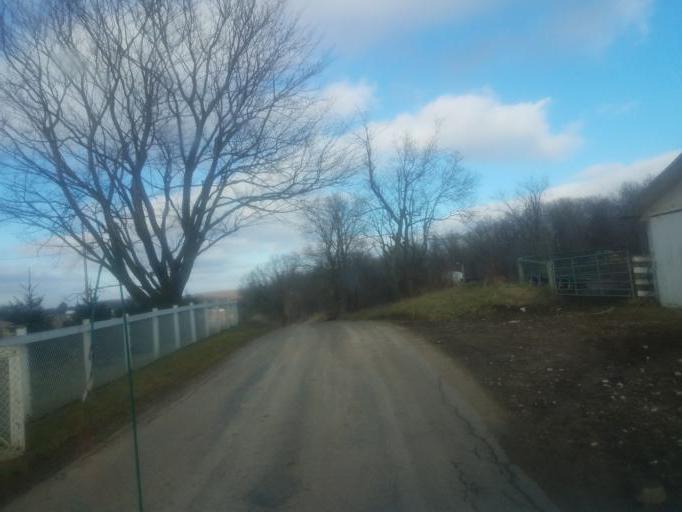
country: US
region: Ohio
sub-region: Sandusky County
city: Bellville
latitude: 40.5846
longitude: -82.3730
